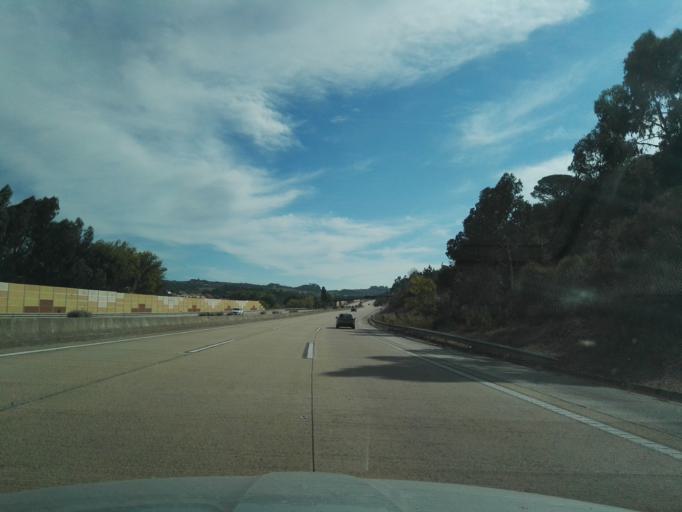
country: PT
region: Lisbon
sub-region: Loures
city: Bucelas
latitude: 38.8987
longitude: -9.1110
